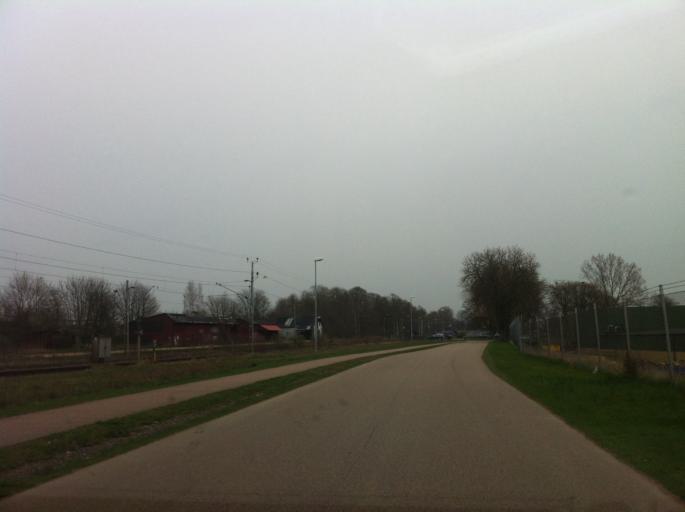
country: SE
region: Skane
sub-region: Svalovs Kommun
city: Kagerod
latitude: 55.9691
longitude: 13.0924
